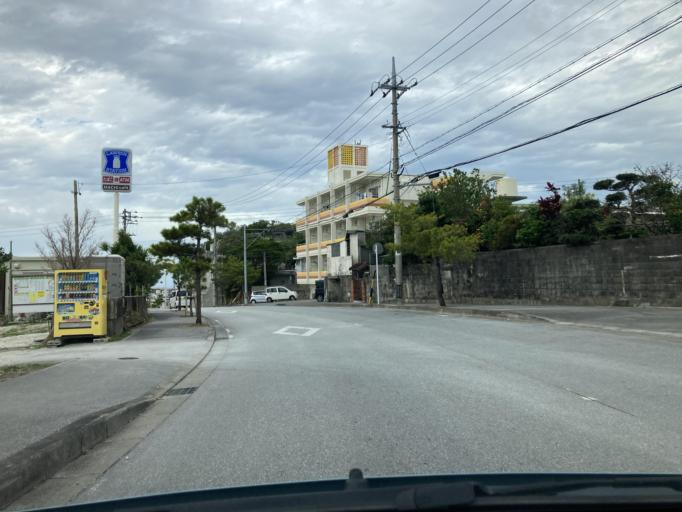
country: JP
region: Okinawa
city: Ginowan
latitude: 26.2178
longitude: 127.7341
